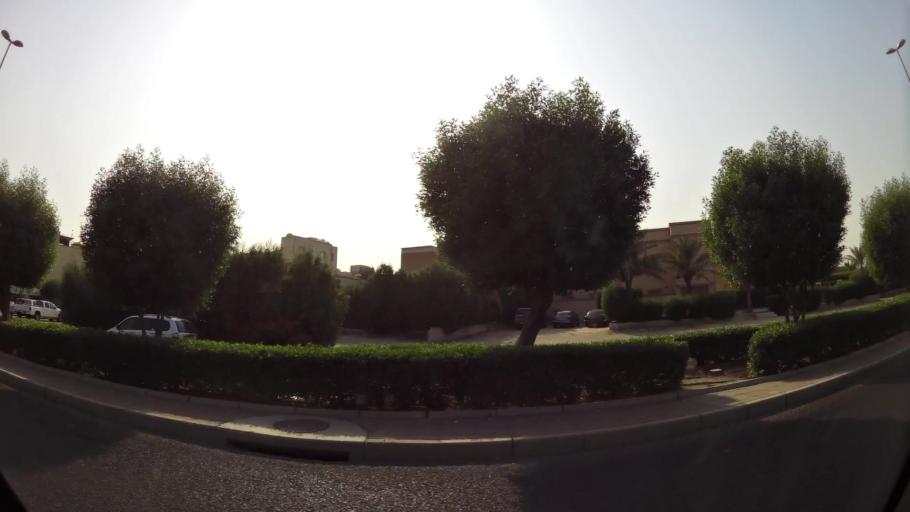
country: KW
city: Al Funaytis
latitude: 29.2155
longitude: 48.0785
